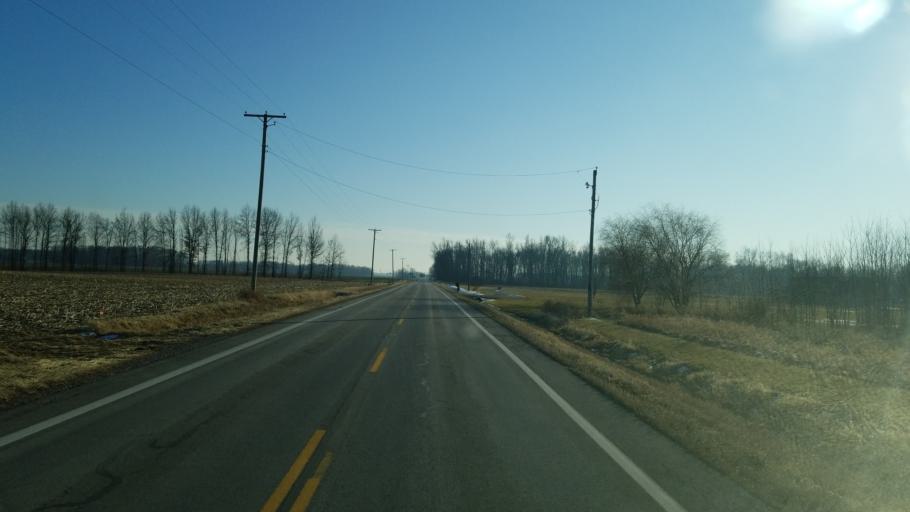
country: US
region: Ohio
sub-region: Seneca County
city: Tiffin
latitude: 41.0187
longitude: -83.0156
